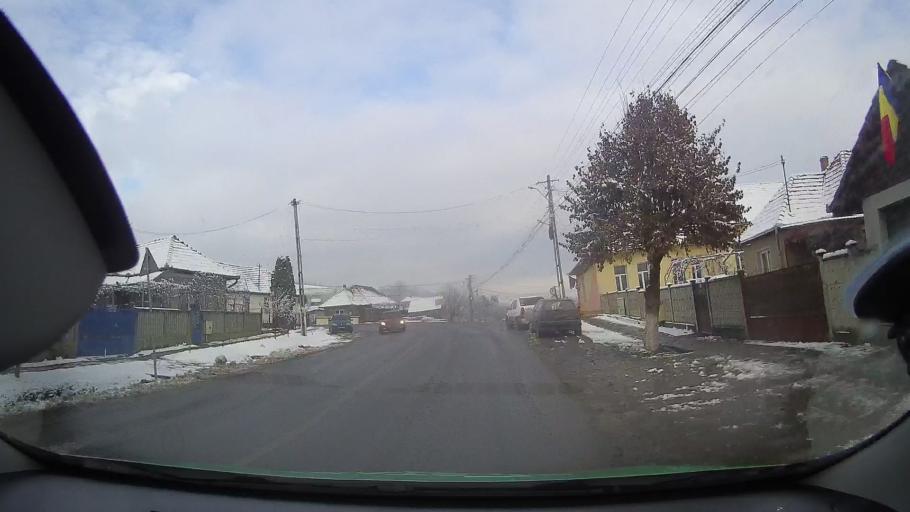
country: RO
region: Mures
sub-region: Comuna Atintis
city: Atintis
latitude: 46.4302
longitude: 24.1049
